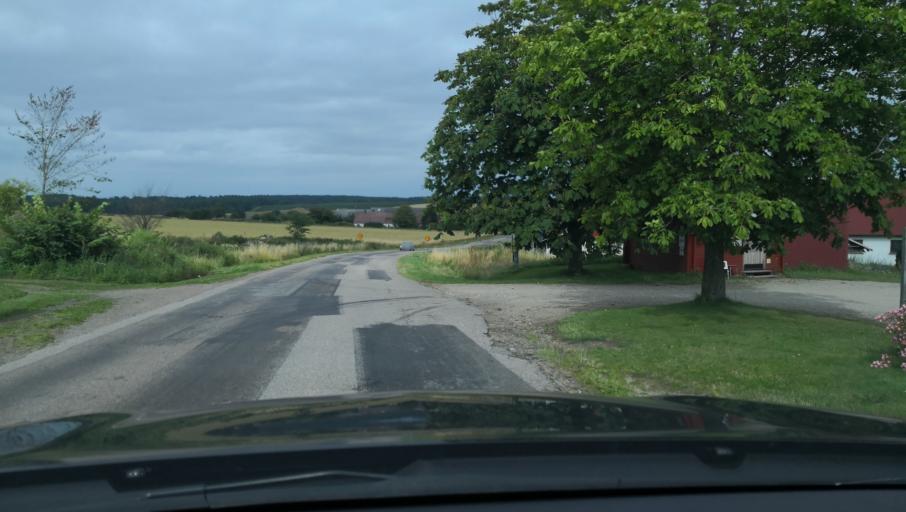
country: SE
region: Skane
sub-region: Simrishamns Kommun
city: Kivik
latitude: 55.6949
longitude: 14.1705
